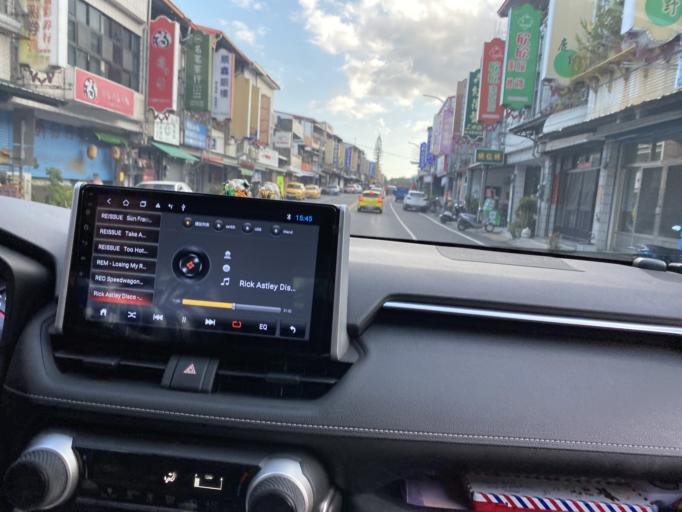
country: TW
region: Taiwan
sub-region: Taitung
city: Taitung
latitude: 22.9125
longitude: 121.1360
